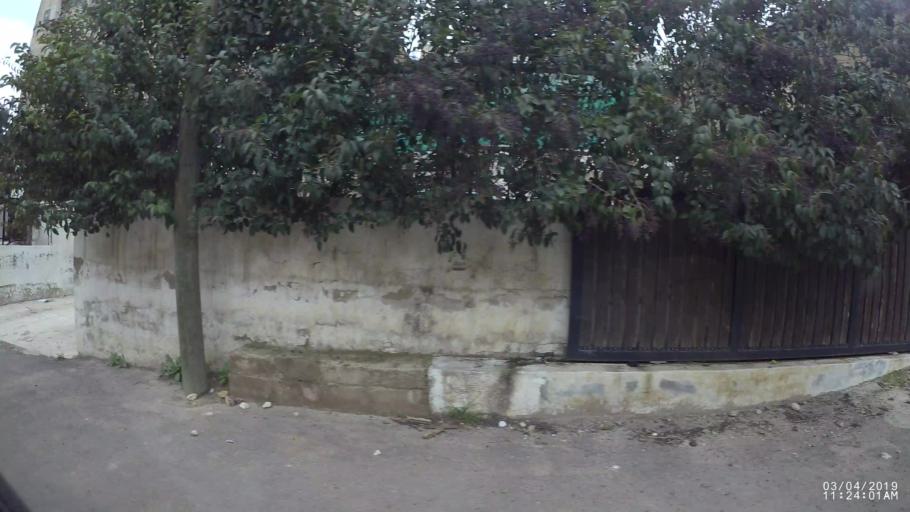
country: JO
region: Amman
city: Wadi as Sir
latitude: 31.9564
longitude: 35.8175
